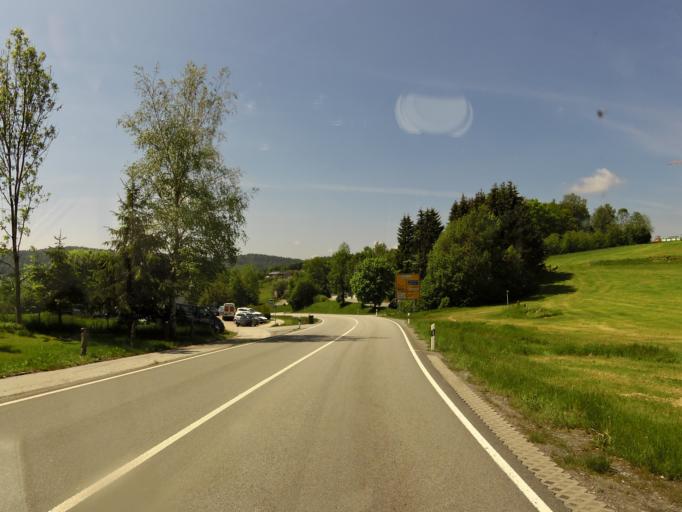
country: DE
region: Bavaria
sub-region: Lower Bavaria
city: Freyung
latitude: 48.8210
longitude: 13.5441
